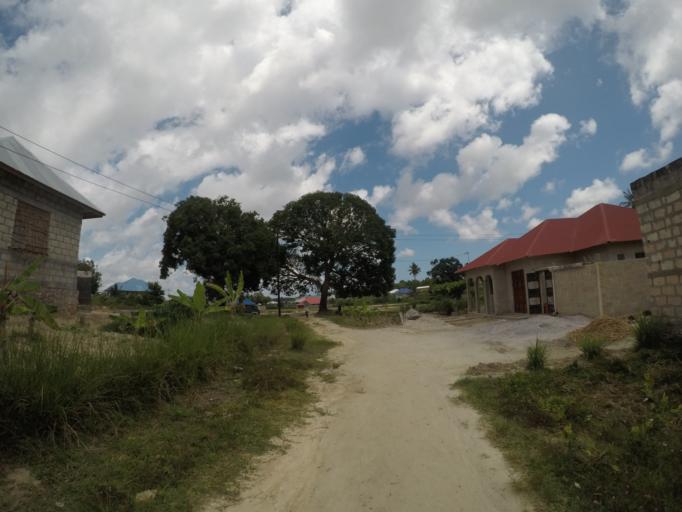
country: TZ
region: Pemba South
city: Chake Chake
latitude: -5.2309
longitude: 39.7829
